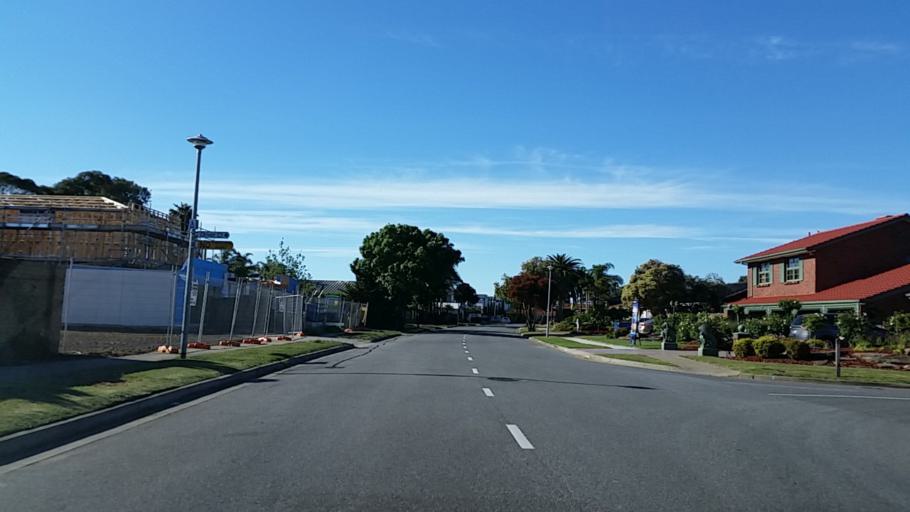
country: AU
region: South Australia
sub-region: Charles Sturt
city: West Lakes Shore
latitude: -34.8706
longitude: 138.4939
